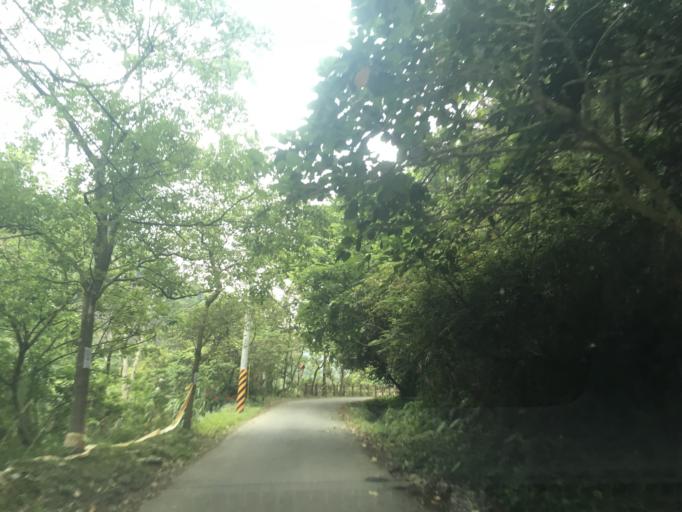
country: TW
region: Taiwan
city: Zhongxing New Village
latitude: 24.0508
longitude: 120.7806
